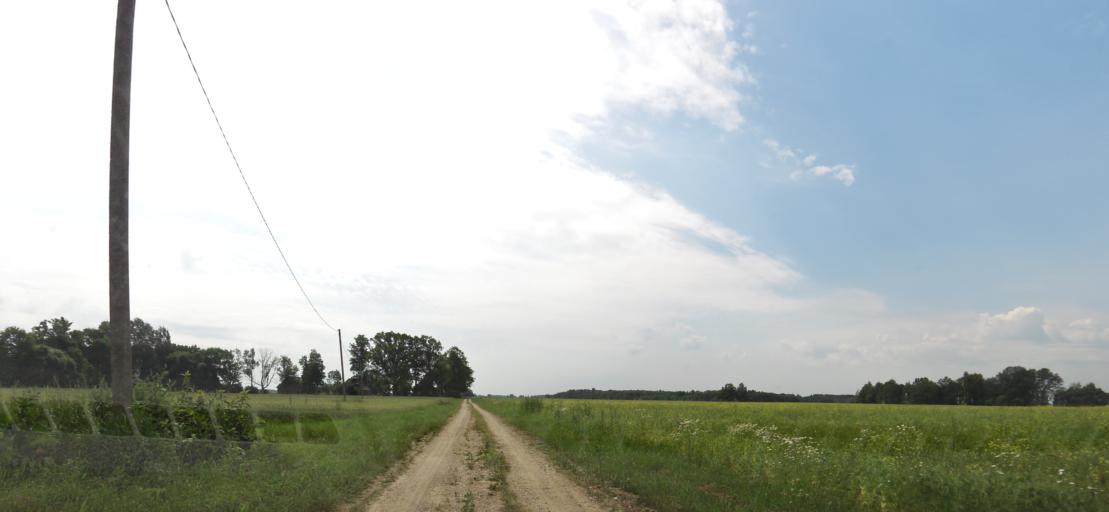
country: LT
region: Panevezys
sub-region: Birzai
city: Birzai
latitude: 56.3228
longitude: 24.7002
